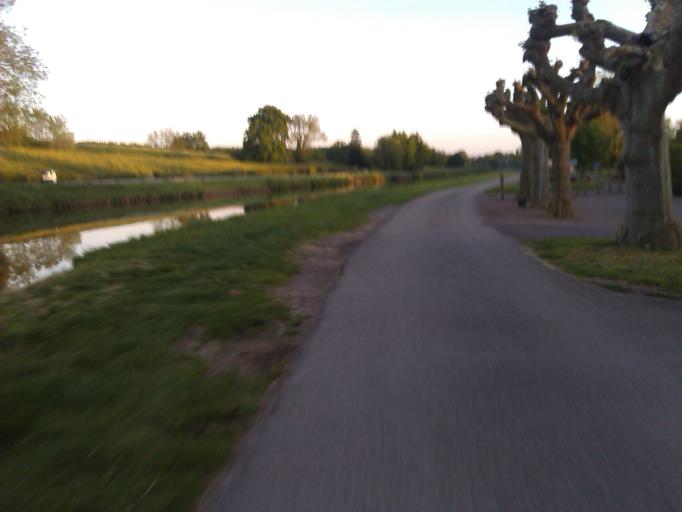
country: FR
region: Bourgogne
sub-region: Departement de Saone-et-Loire
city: Paray-le-Monial
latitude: 46.4512
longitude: 4.1571
